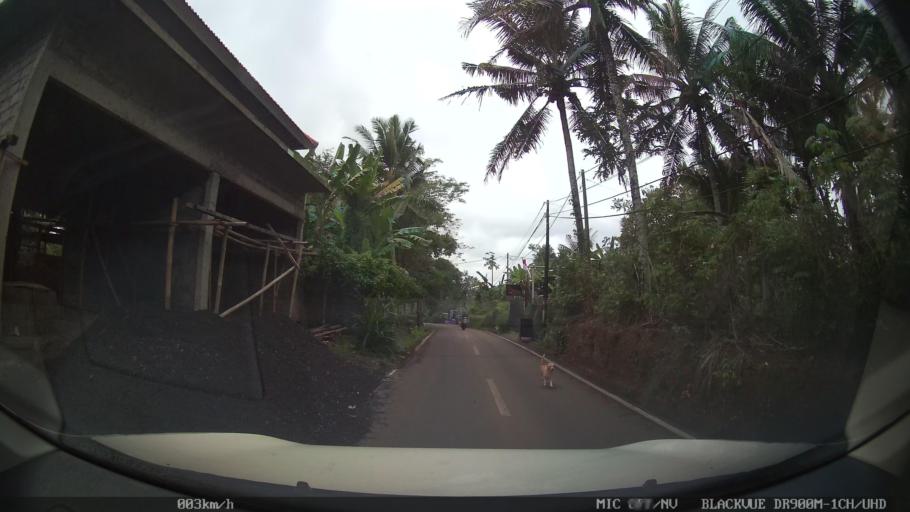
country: ID
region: Bali
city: Banjar Parekan
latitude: -8.5644
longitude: 115.2129
